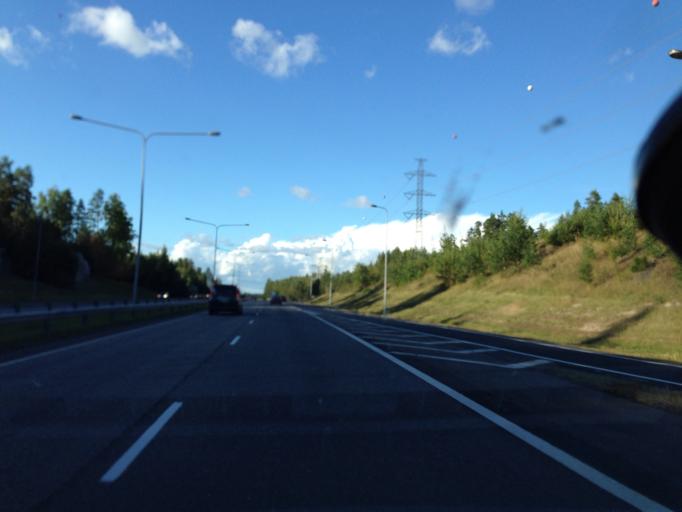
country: FI
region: Uusimaa
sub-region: Helsinki
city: Vantaa
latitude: 60.3260
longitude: 24.9982
